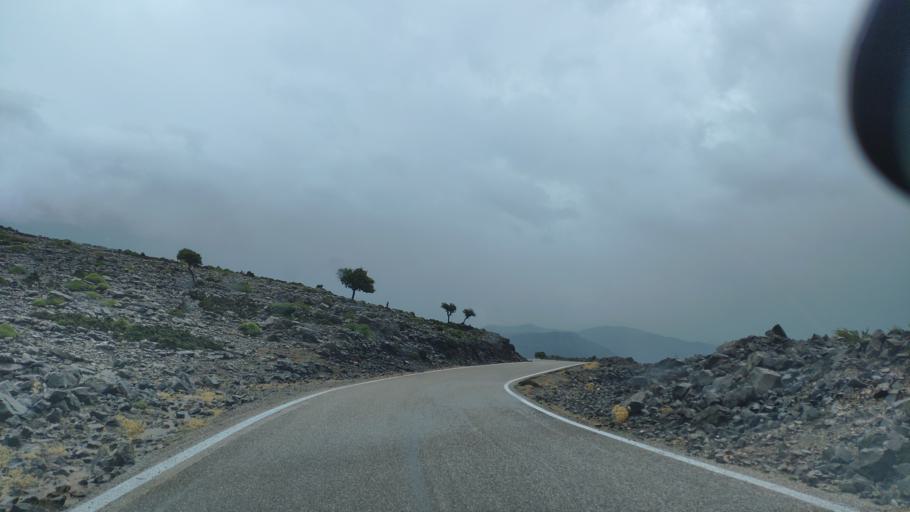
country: GR
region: West Greece
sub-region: Nomos Aitolias kai Akarnanias
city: Krikellos
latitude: 39.0753
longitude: 21.3957
